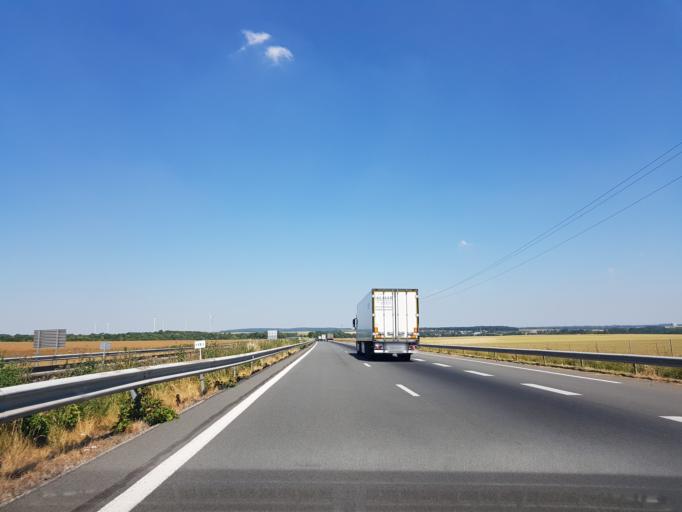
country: FR
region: Nord-Pas-de-Calais
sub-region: Departement du Nord
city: Marcoing
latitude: 50.0960
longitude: 3.1690
